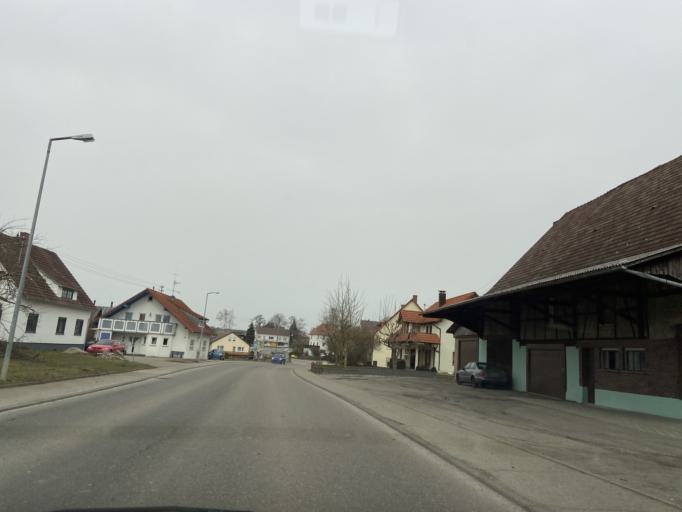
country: DE
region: Baden-Wuerttemberg
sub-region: Tuebingen Region
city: Ostrach
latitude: 47.9306
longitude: 9.3555
